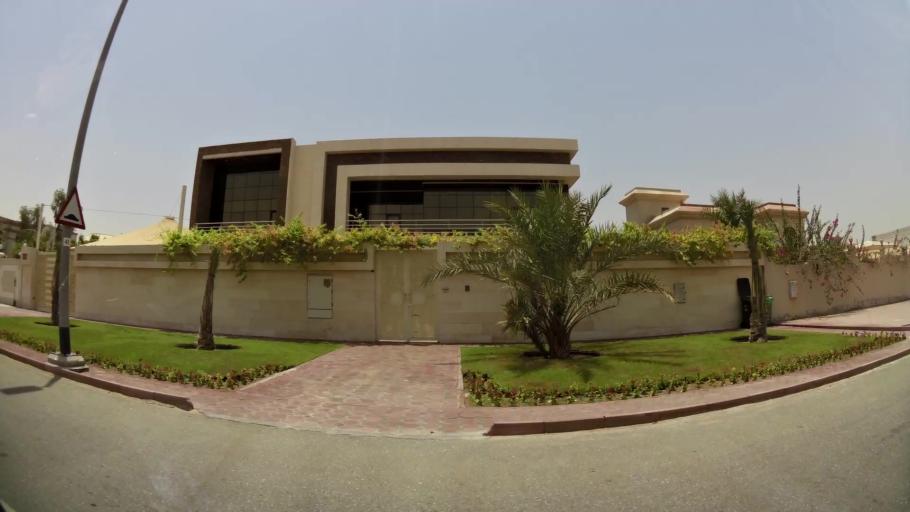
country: AE
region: Ash Shariqah
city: Sharjah
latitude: 25.2059
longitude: 55.3838
